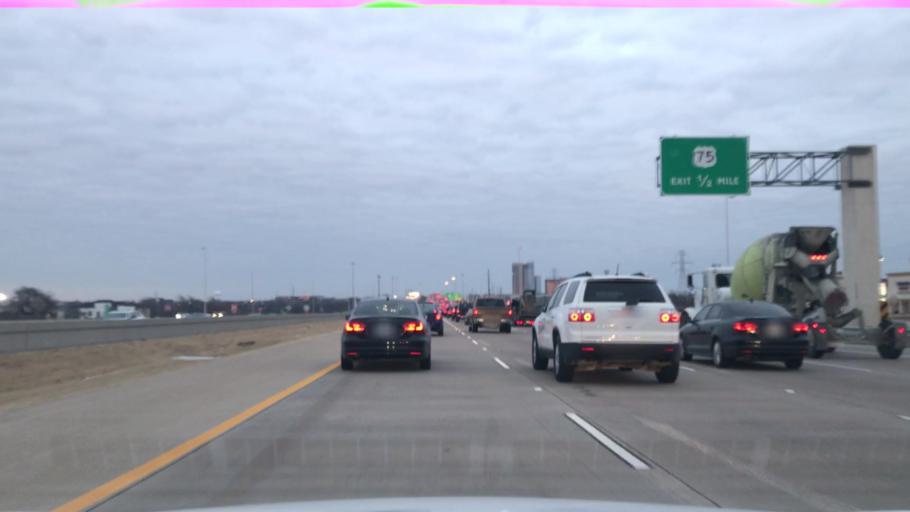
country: US
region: Texas
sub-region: Collin County
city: Plano
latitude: 33.0037
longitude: -96.7243
